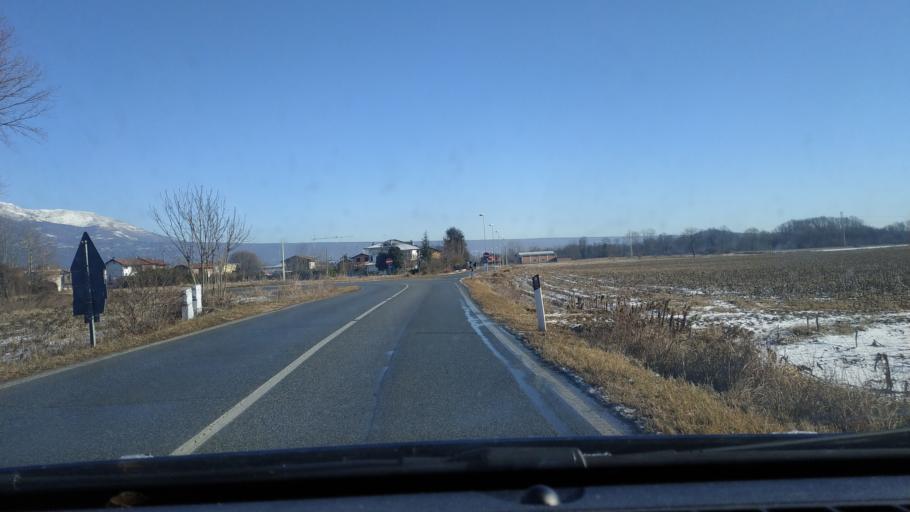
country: IT
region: Piedmont
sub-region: Provincia di Torino
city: Loranze
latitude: 45.4367
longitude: 7.8083
